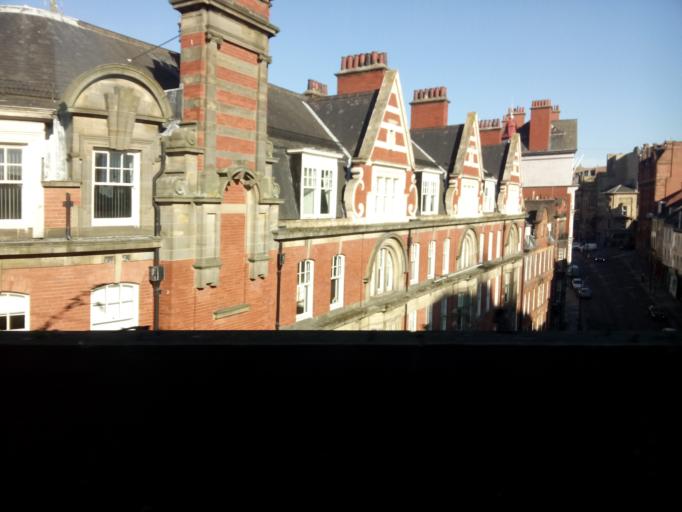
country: GB
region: England
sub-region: Newcastle upon Tyne
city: Newcastle upon Tyne
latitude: 54.9695
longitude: -1.6096
